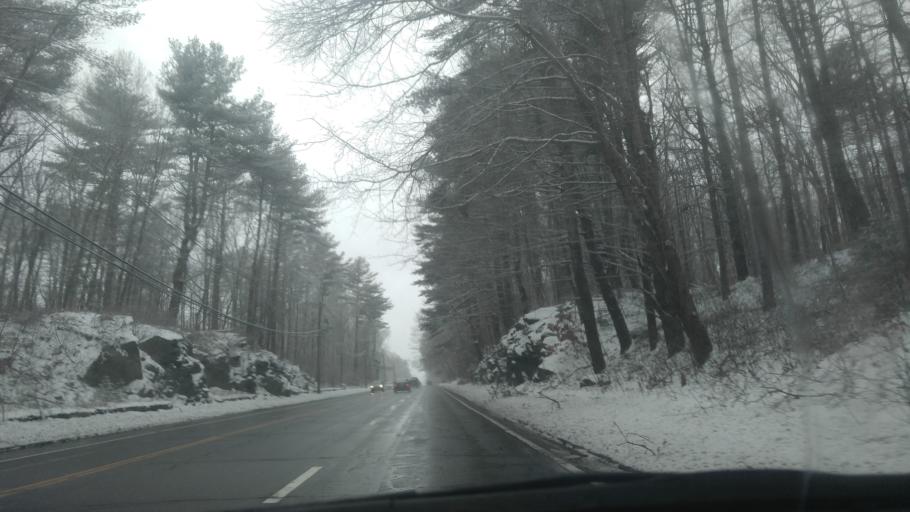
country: US
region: Rhode Island
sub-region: Providence County
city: Foster
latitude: 41.8206
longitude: -71.7077
